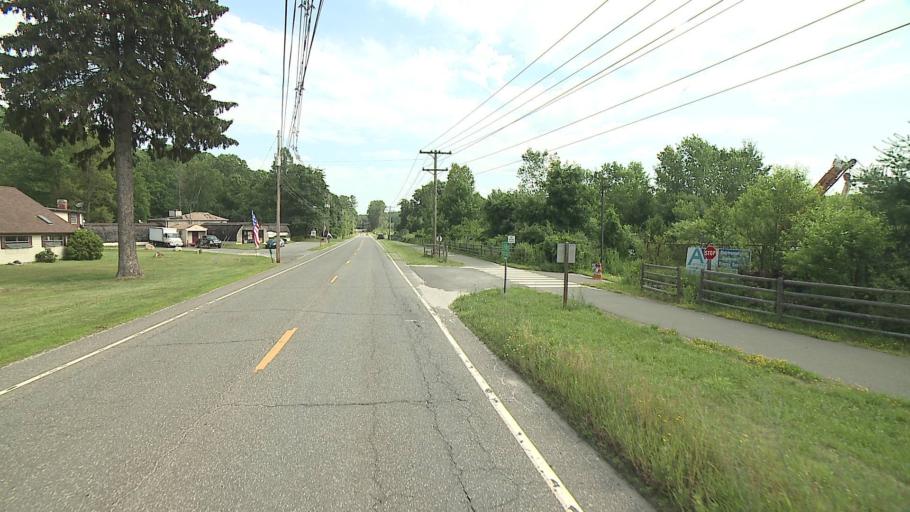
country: US
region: Connecticut
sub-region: Litchfield County
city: Winsted
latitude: 41.8744
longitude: -73.0793
